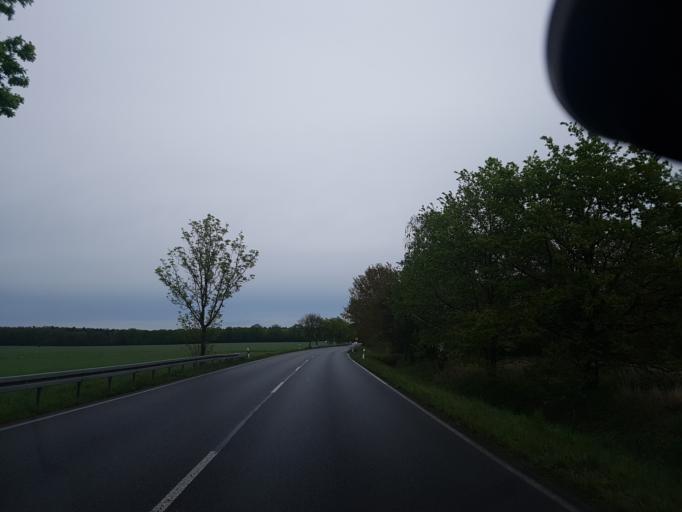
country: DE
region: Brandenburg
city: Neupetershain
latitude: 51.6066
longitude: 14.1313
